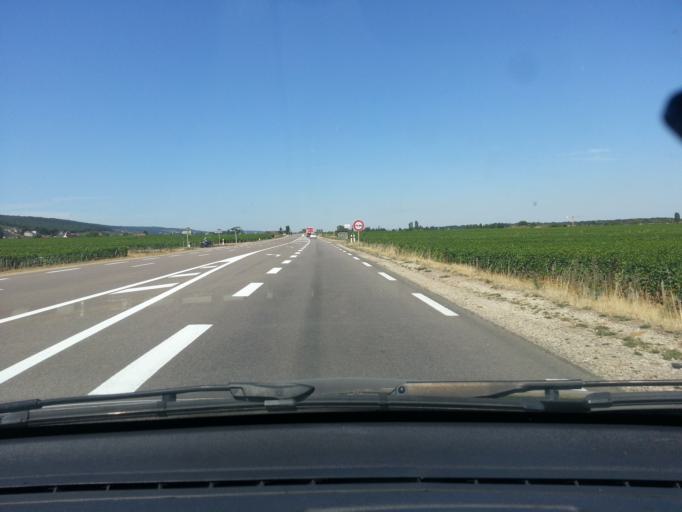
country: FR
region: Bourgogne
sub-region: Departement de la Cote-d'Or
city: Gevrey-Chambertin
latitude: 47.1866
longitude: 4.9673
